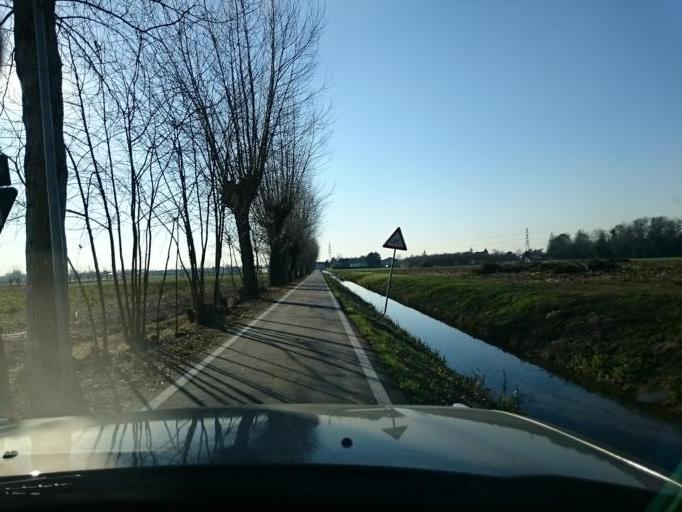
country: IT
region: Veneto
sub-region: Provincia di Venezia
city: Mira Taglio
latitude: 45.4280
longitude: 12.1181
